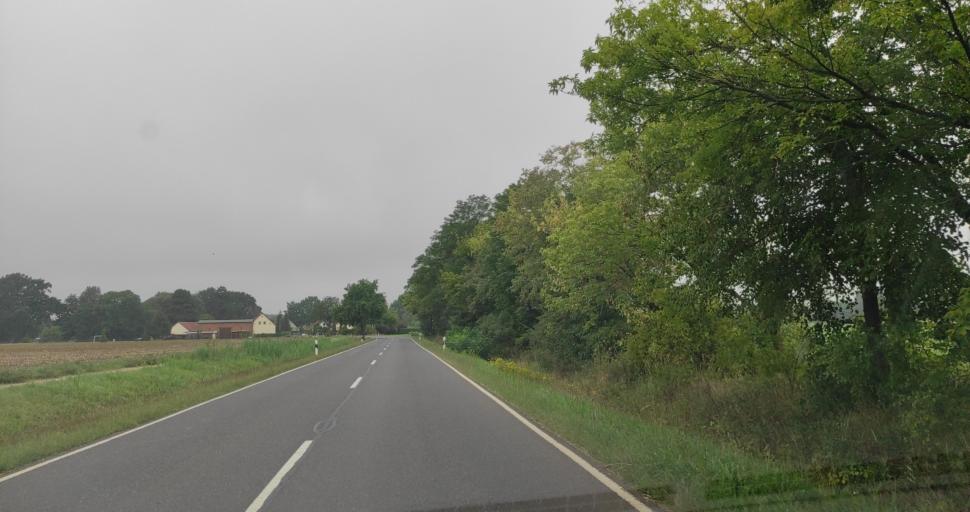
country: DE
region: Brandenburg
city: Forst
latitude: 51.6898
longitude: 14.6158
